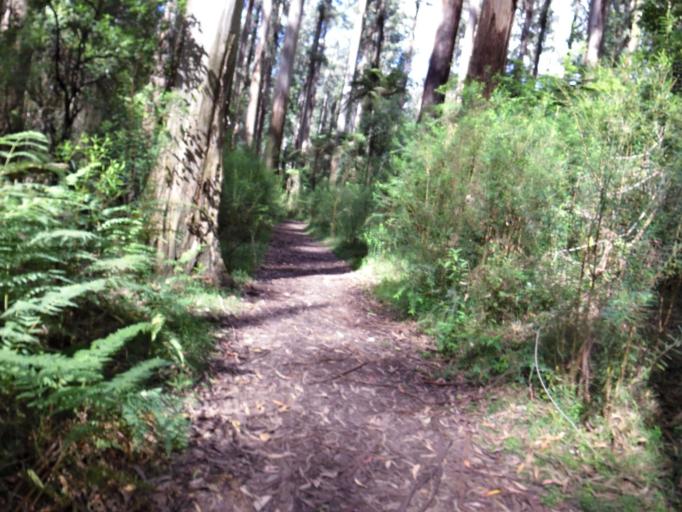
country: AU
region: Victoria
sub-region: Yarra Ranges
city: Ferny Creek
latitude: -37.8813
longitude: 145.3470
